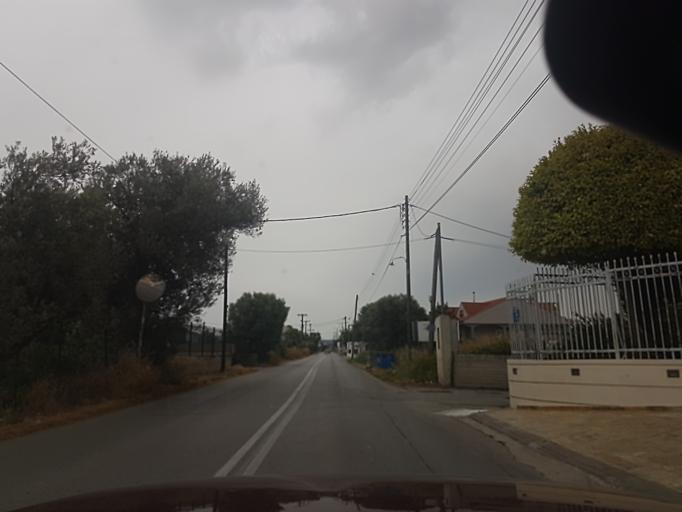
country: GR
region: Central Greece
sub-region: Nomos Evvoias
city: Mytikas
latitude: 38.4648
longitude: 23.6327
